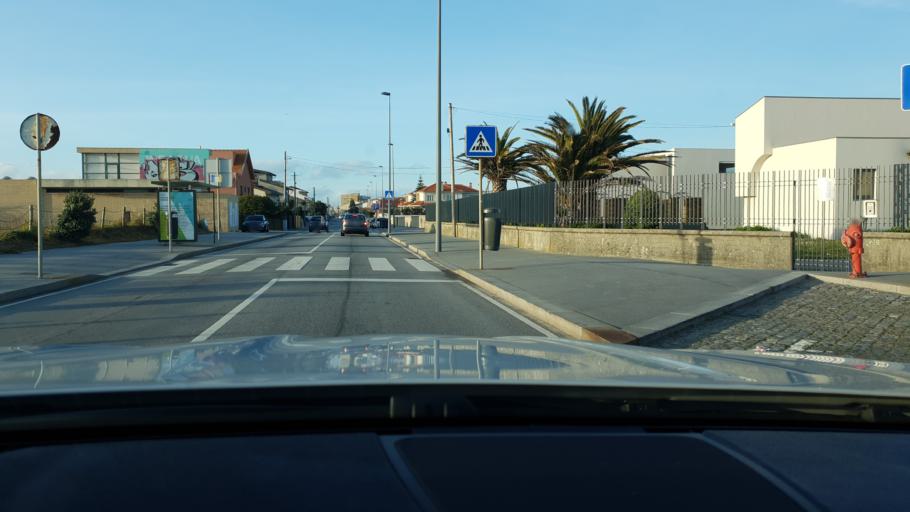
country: PT
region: Porto
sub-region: Matosinhos
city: Lavra
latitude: 41.2343
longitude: -8.7208
